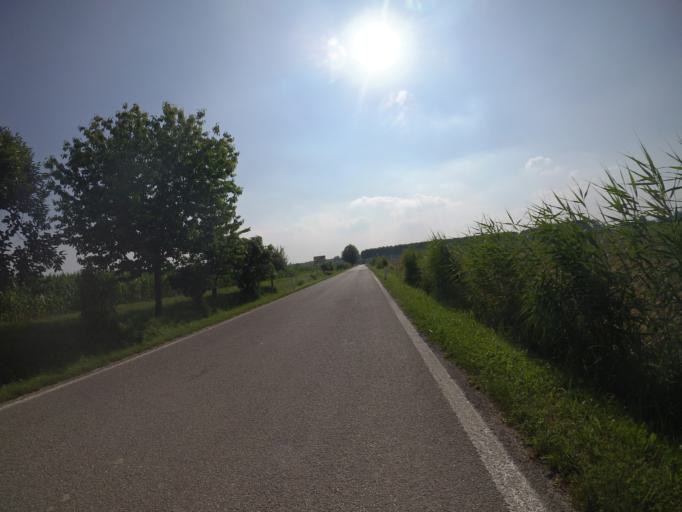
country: IT
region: Friuli Venezia Giulia
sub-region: Provincia di Udine
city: Camino al Tagliamento
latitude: 45.9198
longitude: 12.9680
